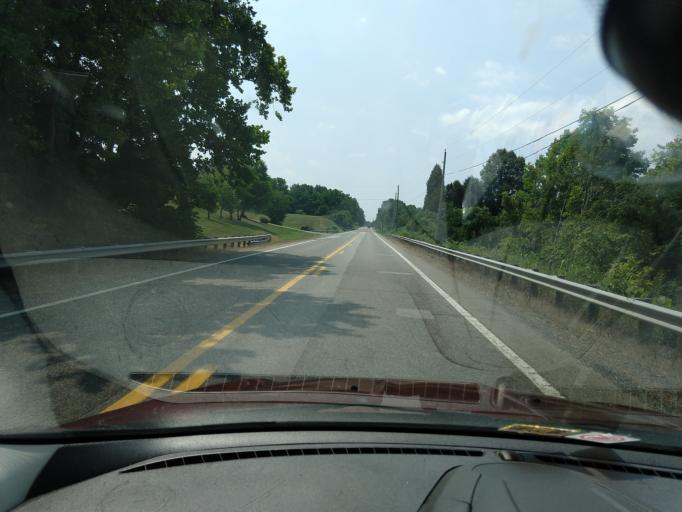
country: US
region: West Virginia
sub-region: Jackson County
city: Ripley
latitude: 38.8523
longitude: -81.8009
